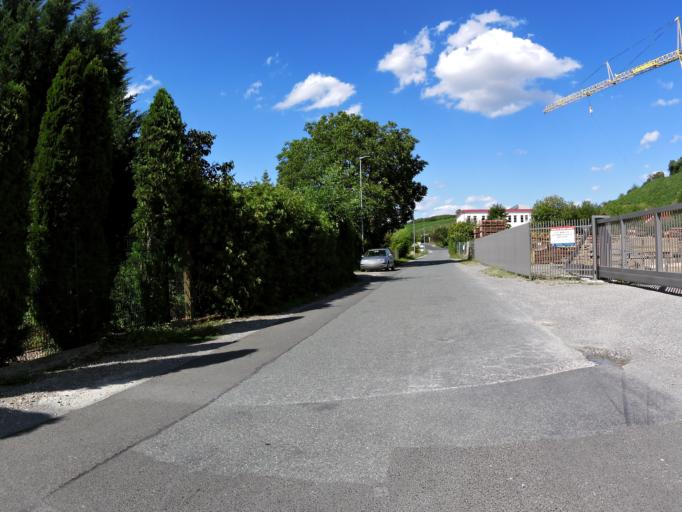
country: DE
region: Bavaria
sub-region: Regierungsbezirk Unterfranken
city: Segnitz
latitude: 49.6778
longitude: 10.1527
